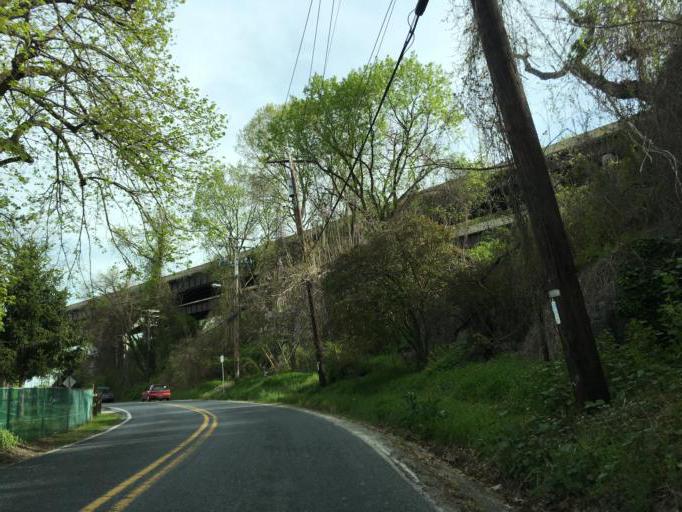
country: US
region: Maryland
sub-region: Howard County
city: Elkridge
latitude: 39.2203
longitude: -76.7131
